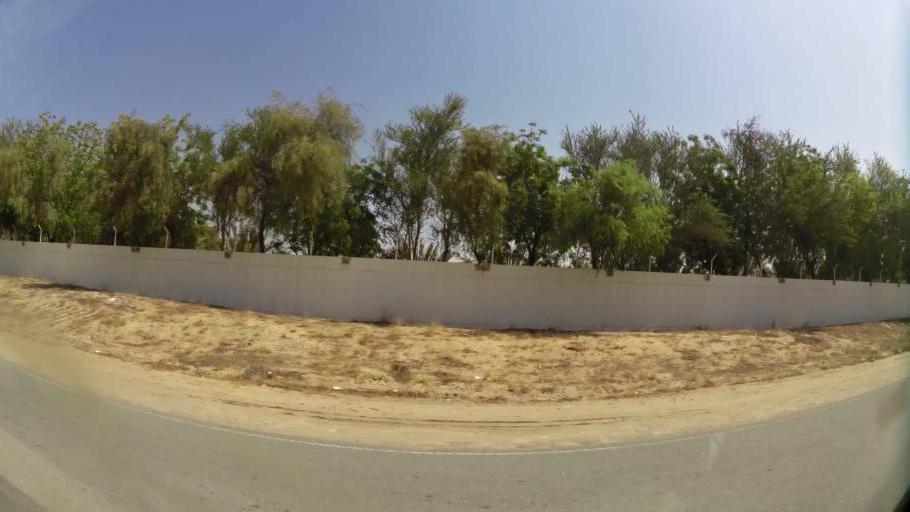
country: AE
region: Ajman
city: Ajman
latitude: 25.3945
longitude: 55.5351
